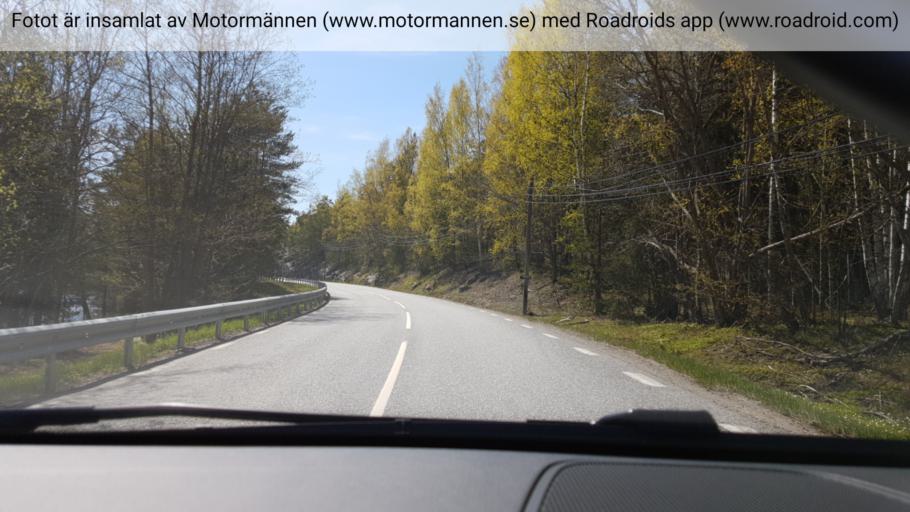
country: SE
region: Stockholm
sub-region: Nynashamns Kommun
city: Nynashamn
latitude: 58.9734
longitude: 18.0700
